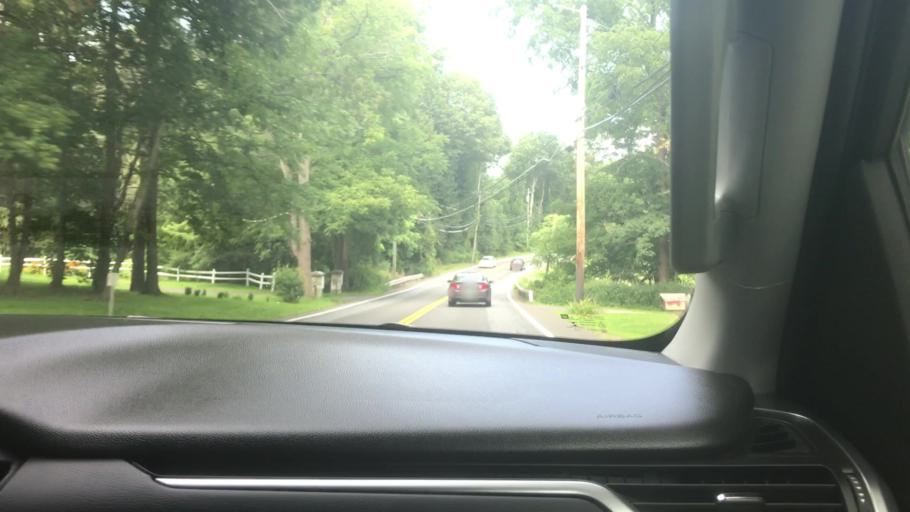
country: US
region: New York
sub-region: Dutchess County
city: Dover Plains
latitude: 41.8670
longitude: -73.5452
